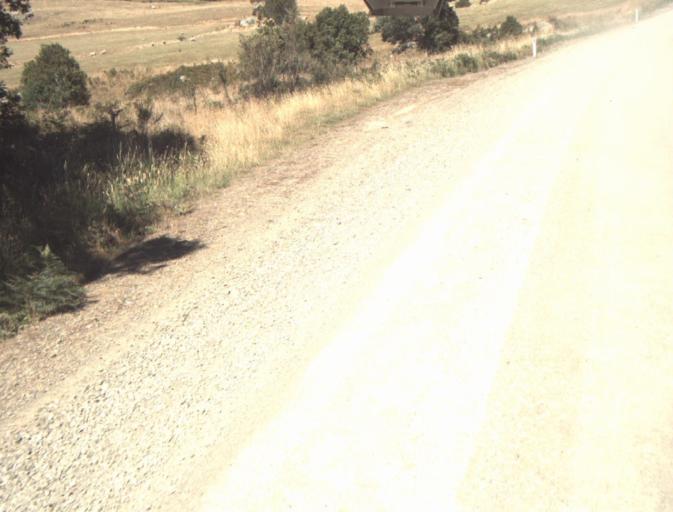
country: AU
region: Tasmania
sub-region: Dorset
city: Scottsdale
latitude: -41.3429
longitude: 147.4349
